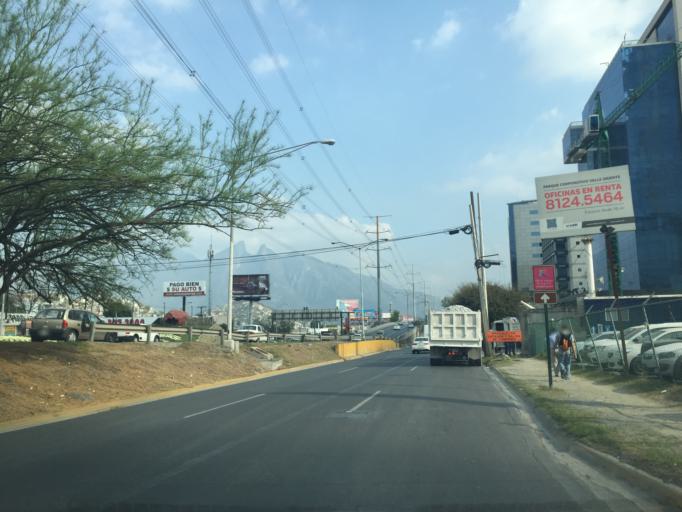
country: MX
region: Nuevo Leon
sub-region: Monterrey
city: Monterrey
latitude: 25.6429
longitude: -100.3201
